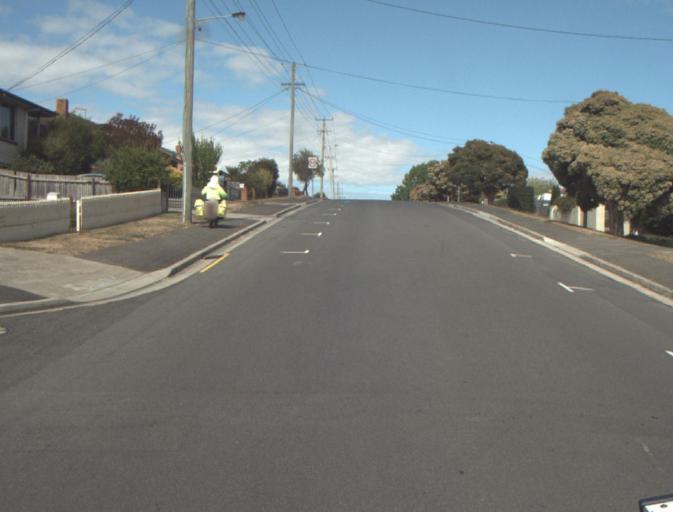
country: AU
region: Tasmania
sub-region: Launceston
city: Summerhill
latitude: -41.4677
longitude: 147.1280
